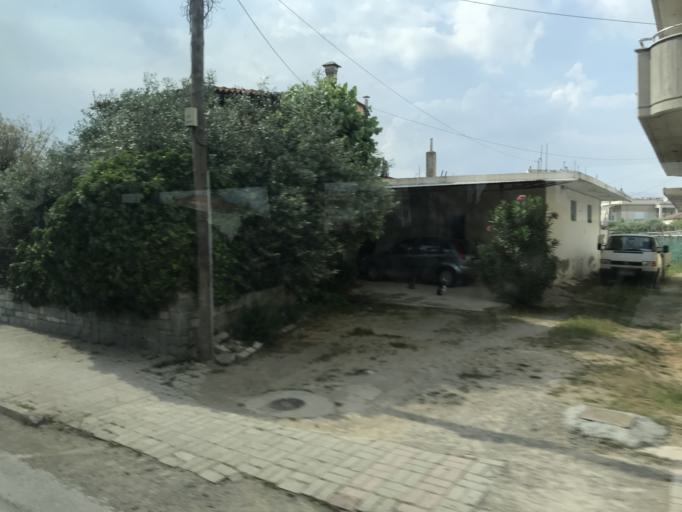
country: GR
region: East Macedonia and Thrace
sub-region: Nomos Evrou
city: Alexandroupoli
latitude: 40.8564
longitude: 25.9360
